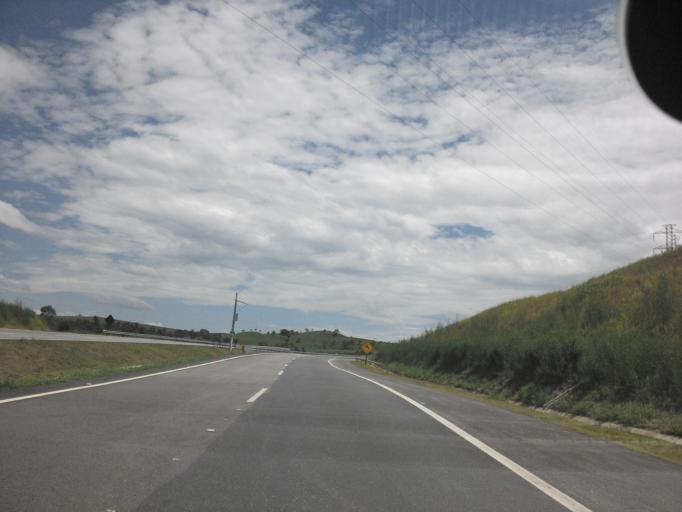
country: BR
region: Sao Paulo
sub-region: Taubate
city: Taubate
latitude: -23.0868
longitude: -45.5574
